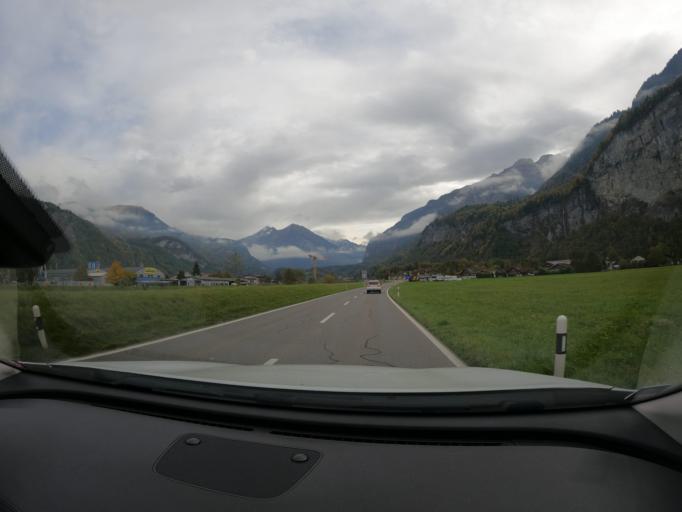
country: CH
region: Bern
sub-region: Interlaken-Oberhasli District
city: Meiringen
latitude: 46.7289
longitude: 8.1676
